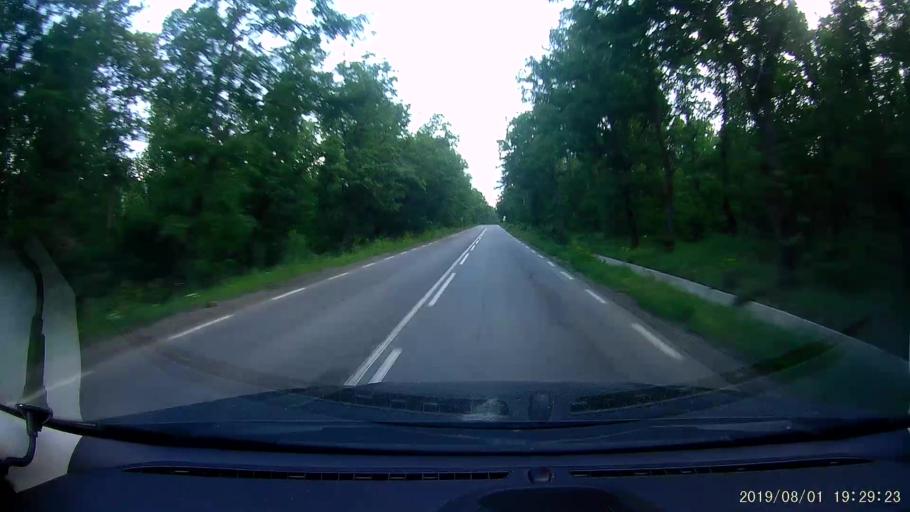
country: BG
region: Burgas
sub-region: Obshtina Sungurlare
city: Sungurlare
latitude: 42.8265
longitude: 26.9079
